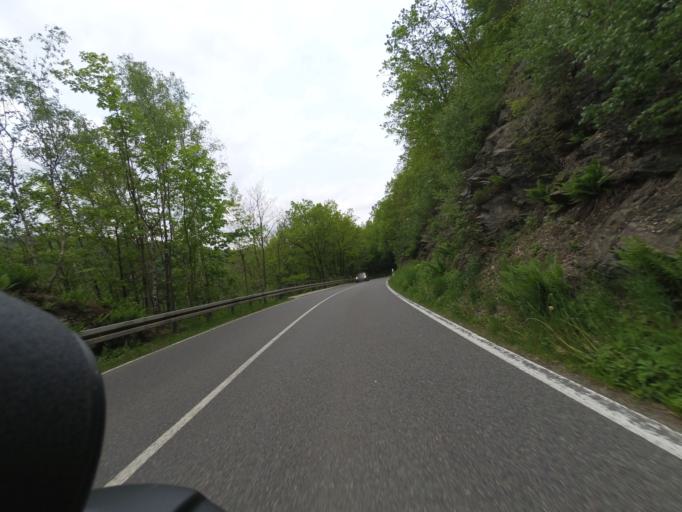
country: DE
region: Saxony
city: Zschopau
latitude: 50.7361
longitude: 13.0635
